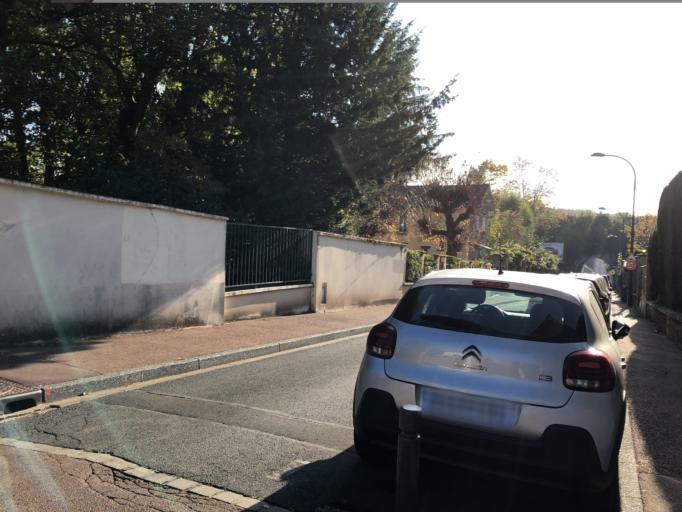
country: FR
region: Ile-de-France
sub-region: Departement des Hauts-de-Seine
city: Chaville
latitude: 48.8106
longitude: 2.1848
